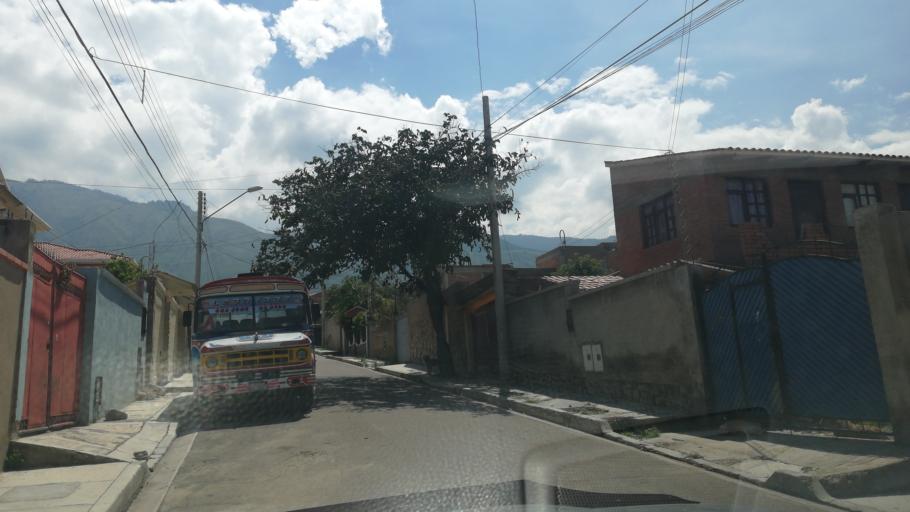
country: BO
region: Cochabamba
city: Cochabamba
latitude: -17.3470
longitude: -66.1761
